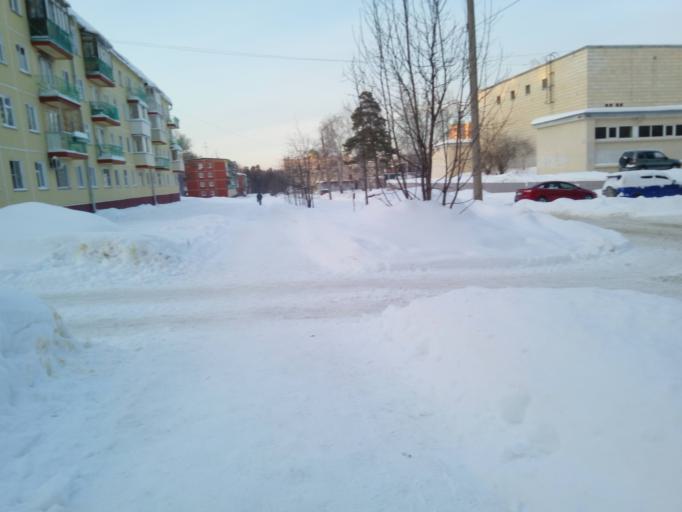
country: RU
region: Novosibirsk
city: Akademgorodok
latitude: 54.8373
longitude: 83.0970
